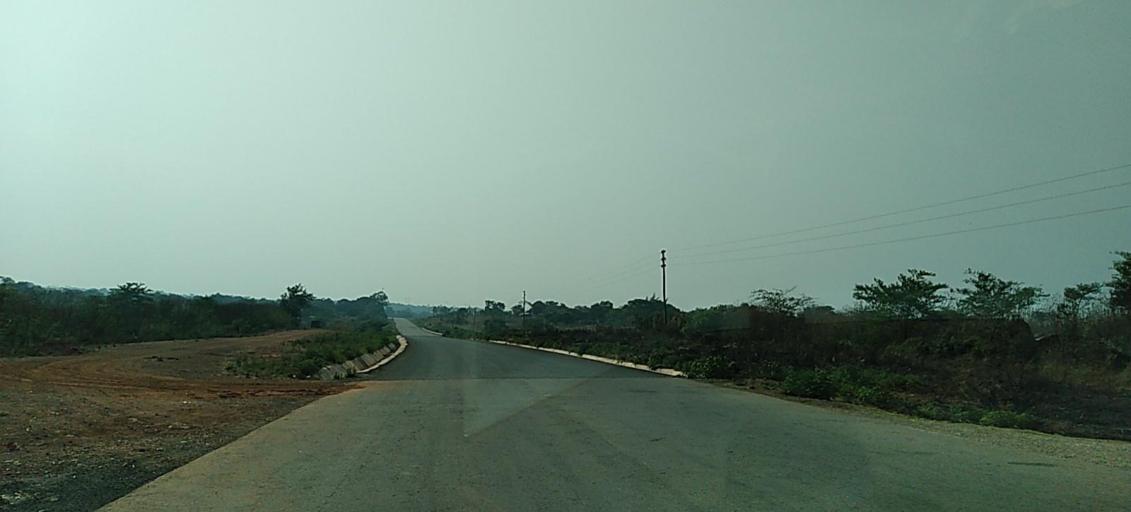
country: ZM
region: North-Western
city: Kansanshi
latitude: -12.3090
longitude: 26.9387
